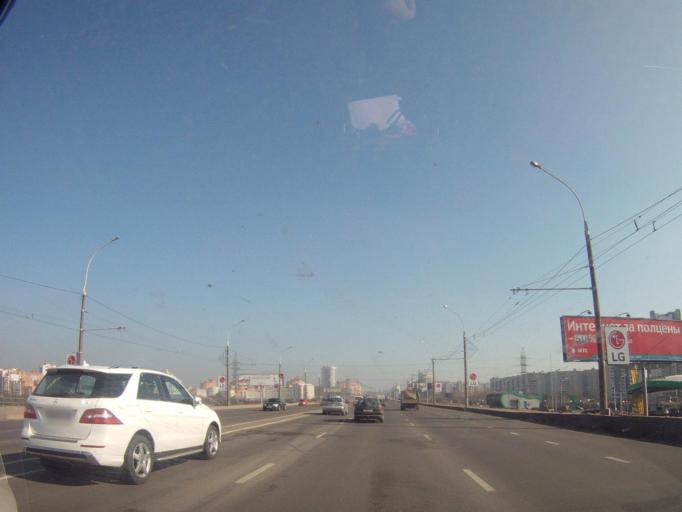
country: BY
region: Minsk
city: Borovlyany
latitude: 53.9408
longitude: 27.6732
